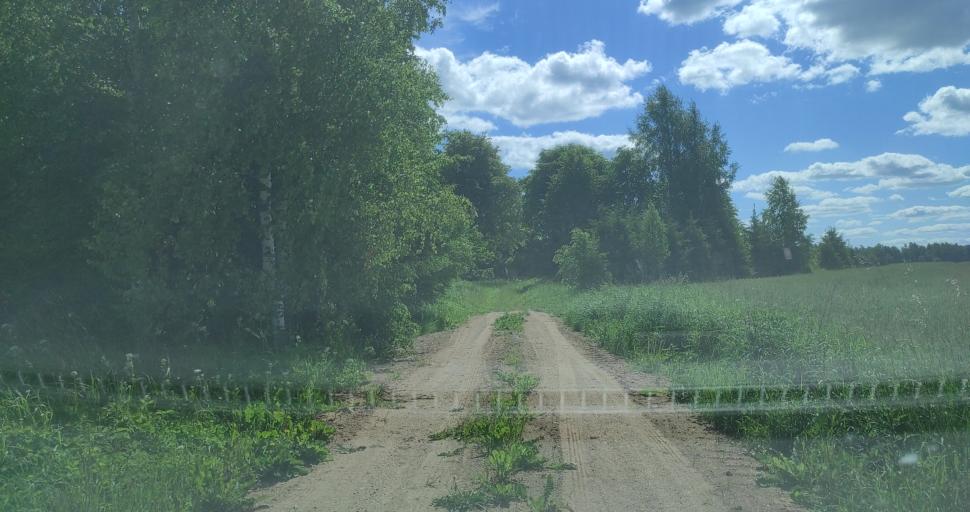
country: LV
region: Alsunga
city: Alsunga
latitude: 56.8964
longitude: 21.7199
